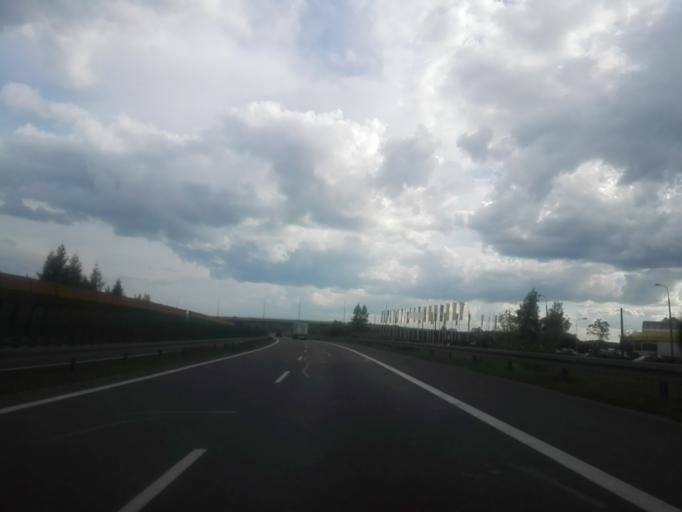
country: PL
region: Masovian Voivodeship
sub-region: Powiat ostrowski
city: Ostrow Mazowiecka
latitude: 52.8132
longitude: 21.8783
